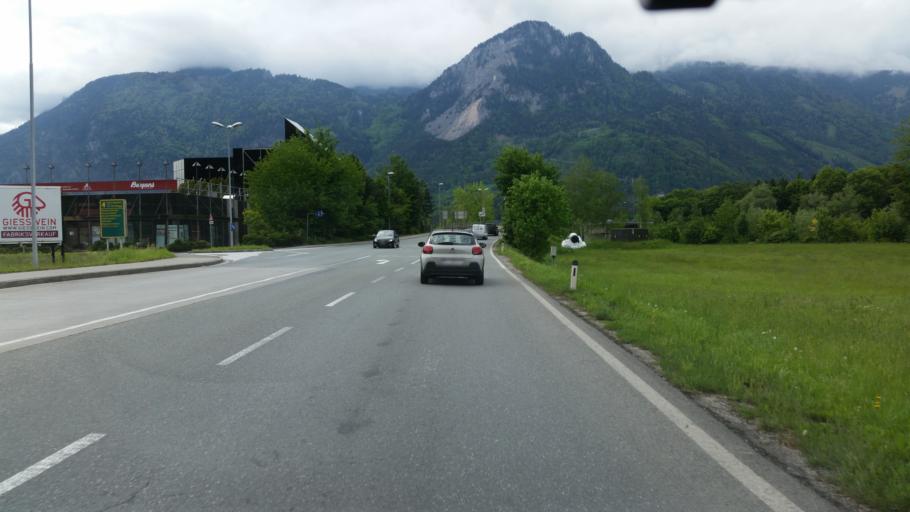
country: AT
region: Tyrol
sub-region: Politischer Bezirk Kufstein
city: Rattenberg
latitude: 47.4373
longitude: 11.8845
